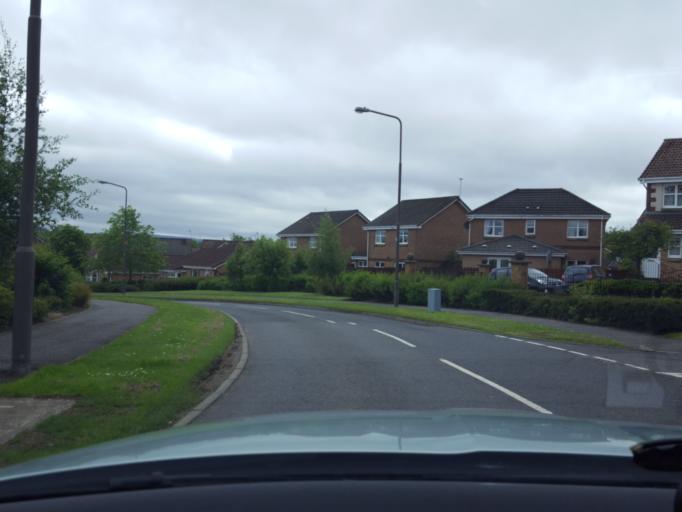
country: GB
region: Scotland
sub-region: West Lothian
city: Broxburn
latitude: 55.9294
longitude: -3.4963
